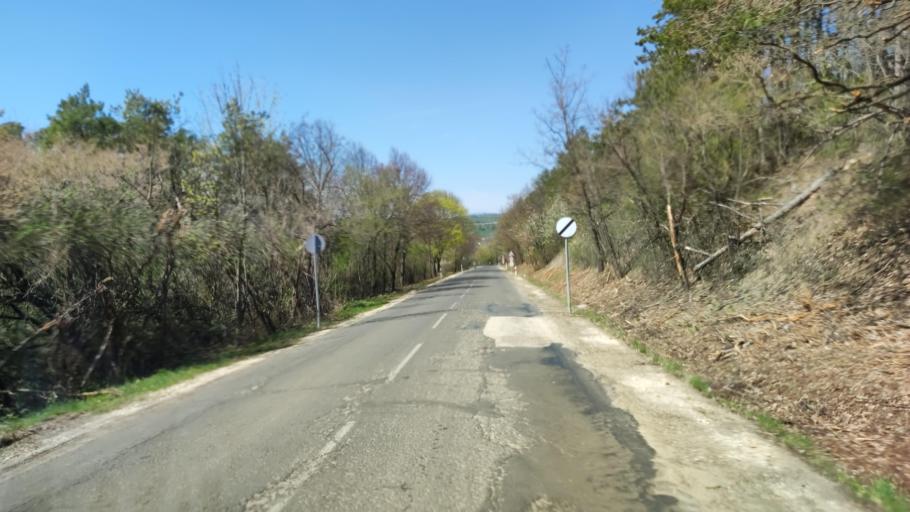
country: HU
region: Pest
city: Kosd
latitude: 47.7936
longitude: 19.1736
